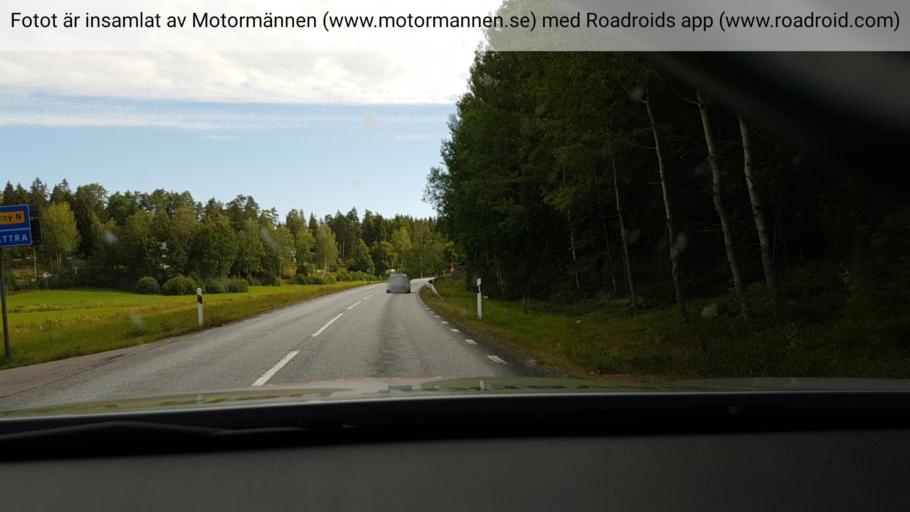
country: SE
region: Stockholm
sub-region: Vaxholms Kommun
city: Resaro
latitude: 59.5327
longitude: 18.4363
